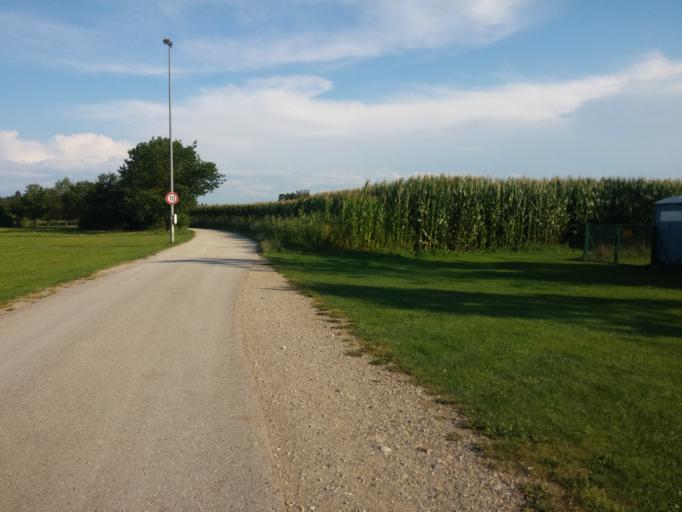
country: DE
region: Bavaria
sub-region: Upper Bavaria
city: Grasbrunn
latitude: 48.0743
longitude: 11.7510
